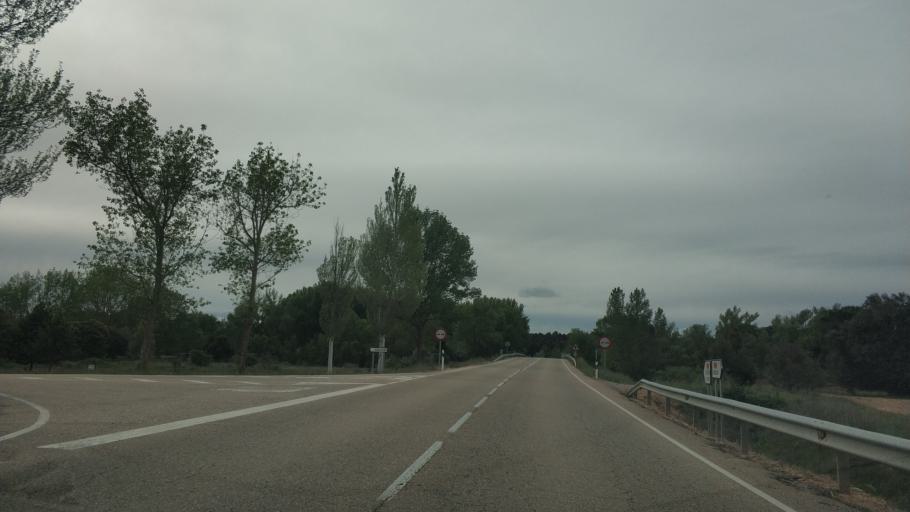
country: ES
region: Castille and Leon
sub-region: Provincia de Soria
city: Bayubas de Abajo
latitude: 41.5013
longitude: -2.8870
